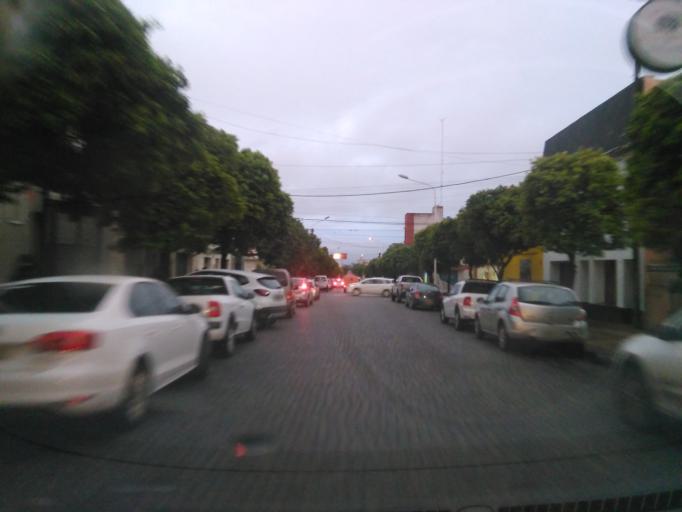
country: AR
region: Buenos Aires
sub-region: Partido de Tandil
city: Tandil
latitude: -37.3249
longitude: -59.1391
